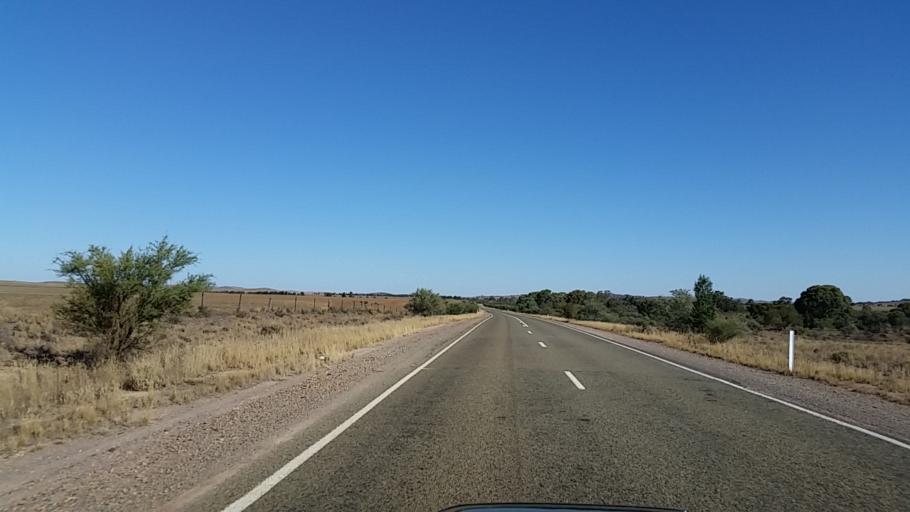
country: AU
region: South Australia
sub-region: Flinders Ranges
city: Quorn
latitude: -32.4503
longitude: 138.5366
